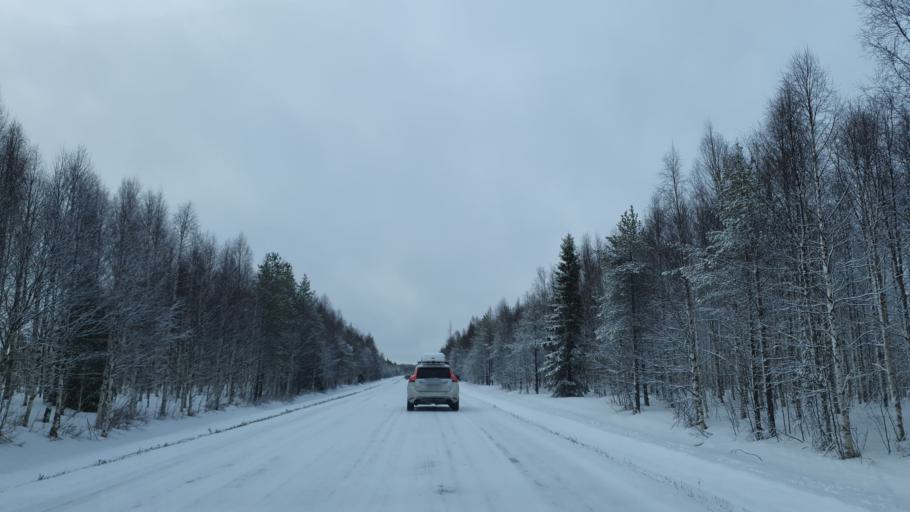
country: FI
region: Lapland
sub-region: Tunturi-Lappi
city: Kittilae
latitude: 67.2677
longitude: 24.8851
